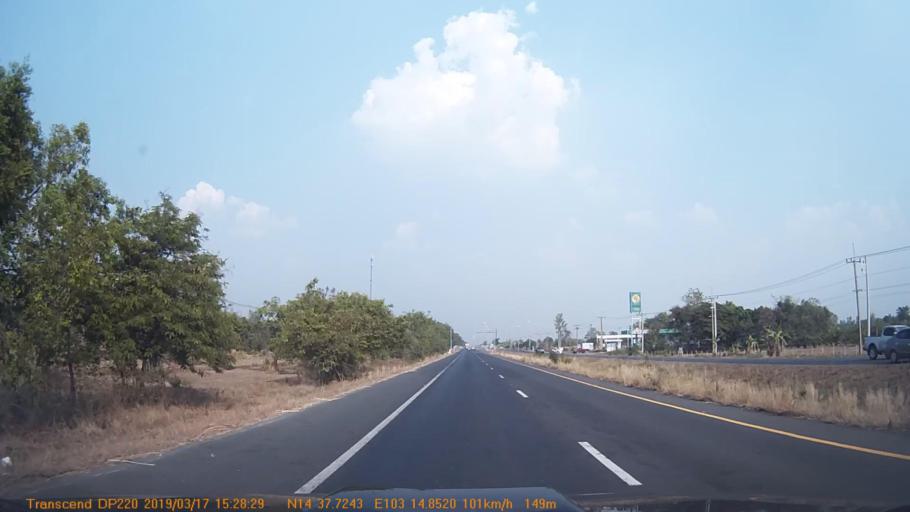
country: TH
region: Buriram
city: Prakhon Chai
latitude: 14.6286
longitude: 103.2480
